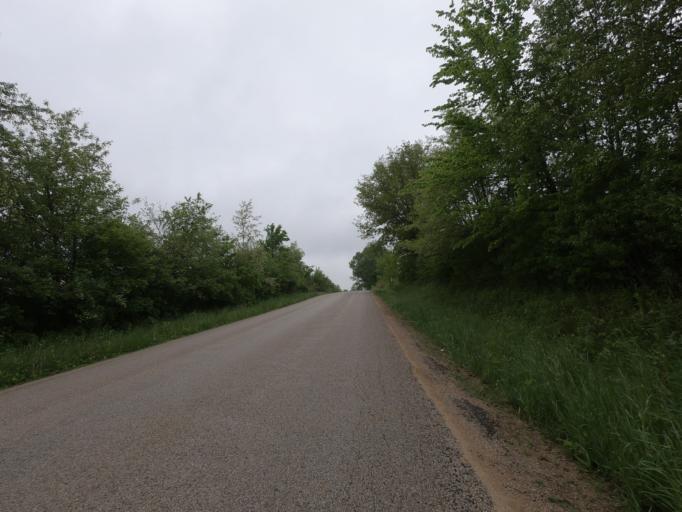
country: US
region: Wisconsin
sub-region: Grant County
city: Hazel Green
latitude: 42.4845
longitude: -90.4897
